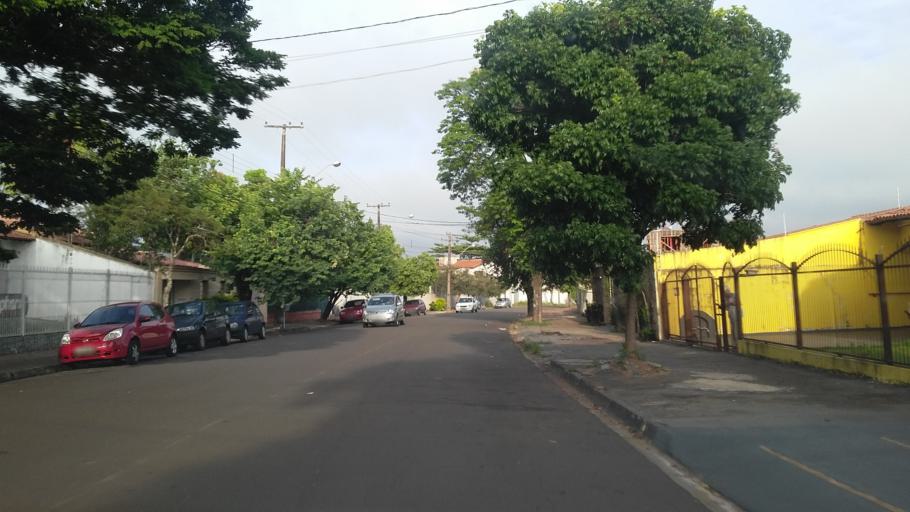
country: BR
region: Parana
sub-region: Londrina
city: Londrina
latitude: -23.2996
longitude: -51.1793
